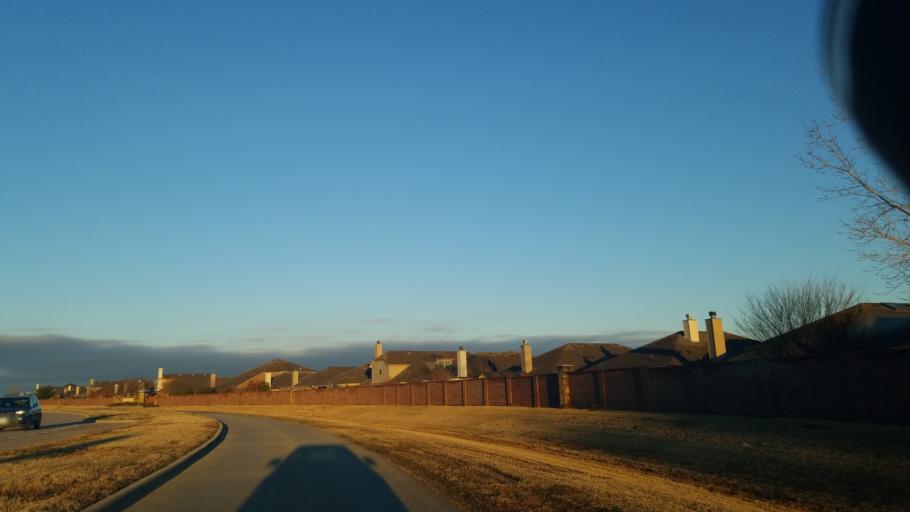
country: US
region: Texas
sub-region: Denton County
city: Denton
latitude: 33.1696
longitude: -97.1607
